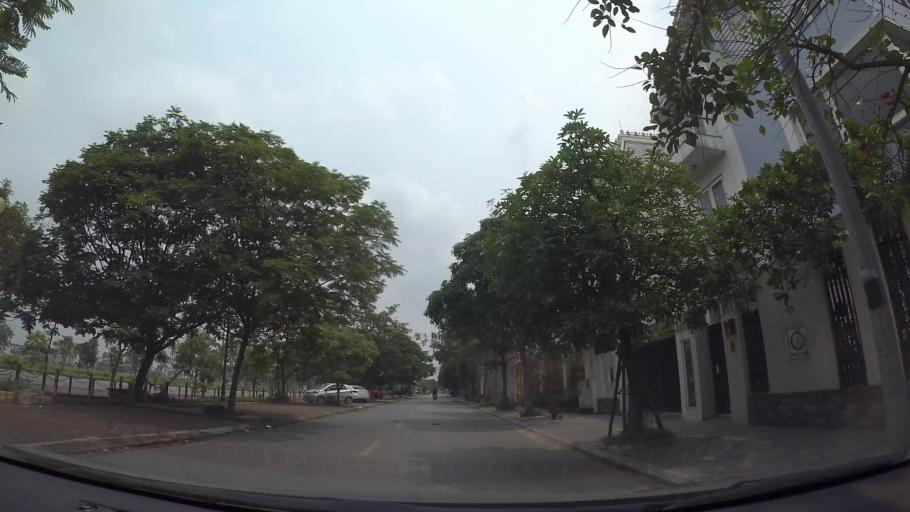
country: VN
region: Ha Noi
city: Trau Quy
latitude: 21.0678
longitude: 105.9109
